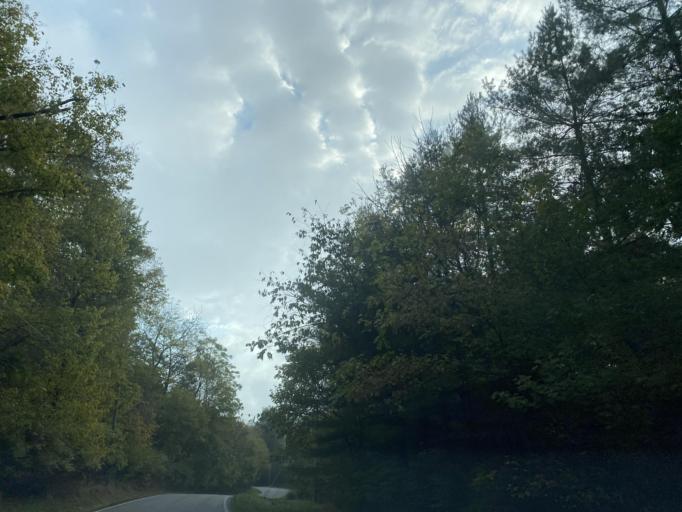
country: US
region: Kentucky
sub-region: Pendleton County
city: Falmouth
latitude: 38.7509
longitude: -84.3289
